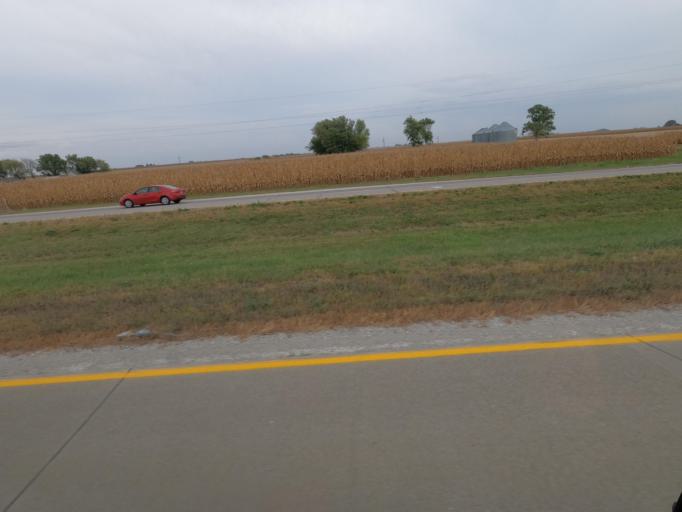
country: US
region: Iowa
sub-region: Jasper County
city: Monroe
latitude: 41.4468
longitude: -93.0216
